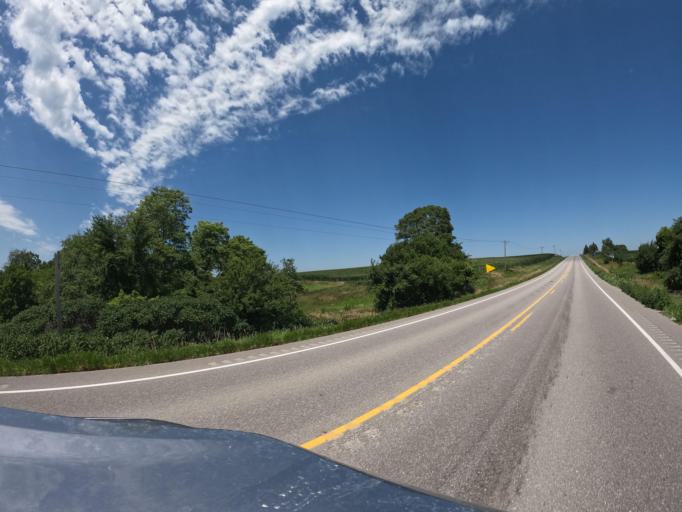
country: US
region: Iowa
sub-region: Keokuk County
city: Sigourney
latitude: 41.4119
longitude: -92.3546
